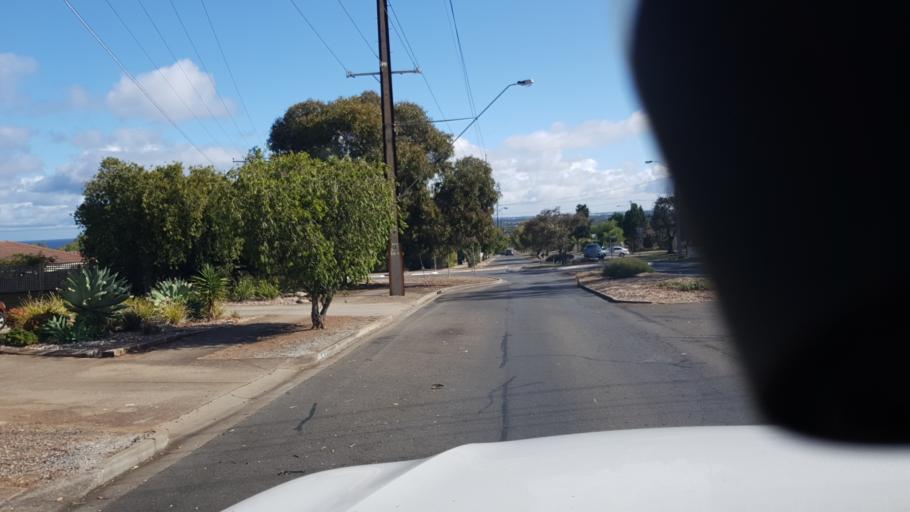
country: AU
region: South Australia
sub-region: Holdfast Bay
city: Seacliff Park
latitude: -35.0353
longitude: 138.5333
